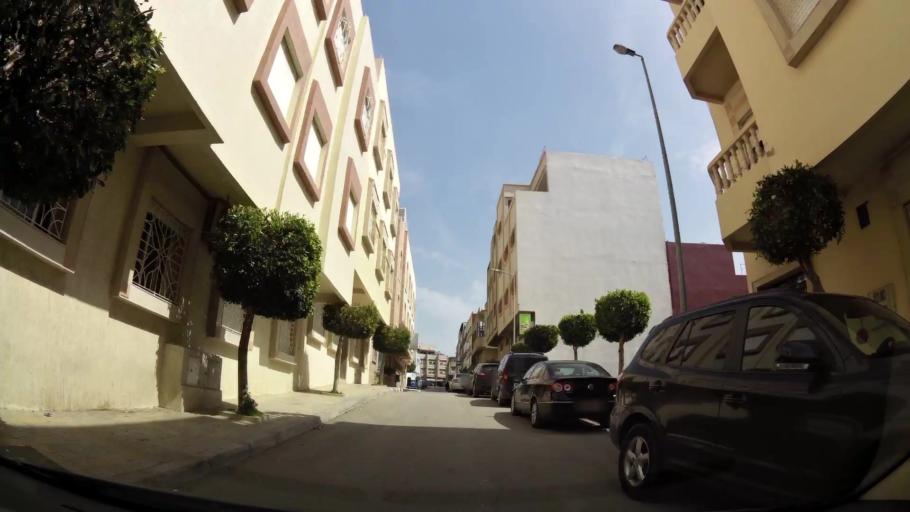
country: MA
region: Tanger-Tetouan
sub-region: Tanger-Assilah
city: Tangier
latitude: 35.7452
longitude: -5.8316
